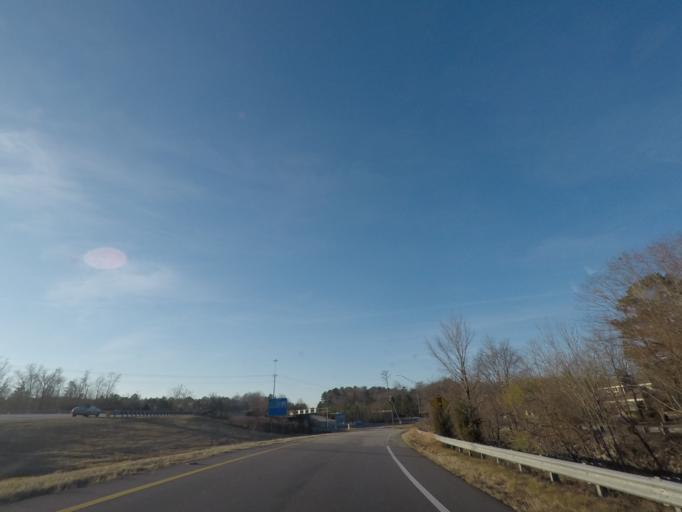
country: US
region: North Carolina
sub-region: Durham County
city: Durham
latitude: 36.0254
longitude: -78.9522
